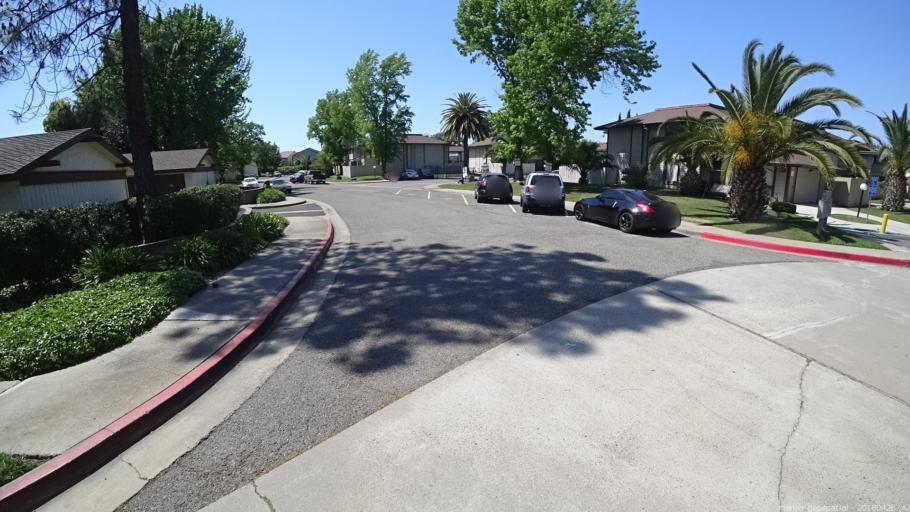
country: US
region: California
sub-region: Yolo County
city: West Sacramento
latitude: 38.5517
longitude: -121.5394
